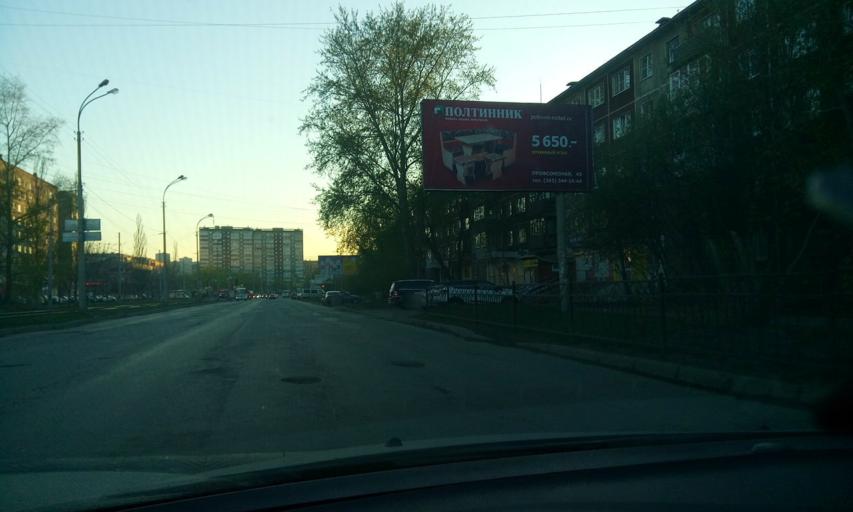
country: RU
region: Sverdlovsk
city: Yekaterinburg
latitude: 56.8351
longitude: 60.6884
